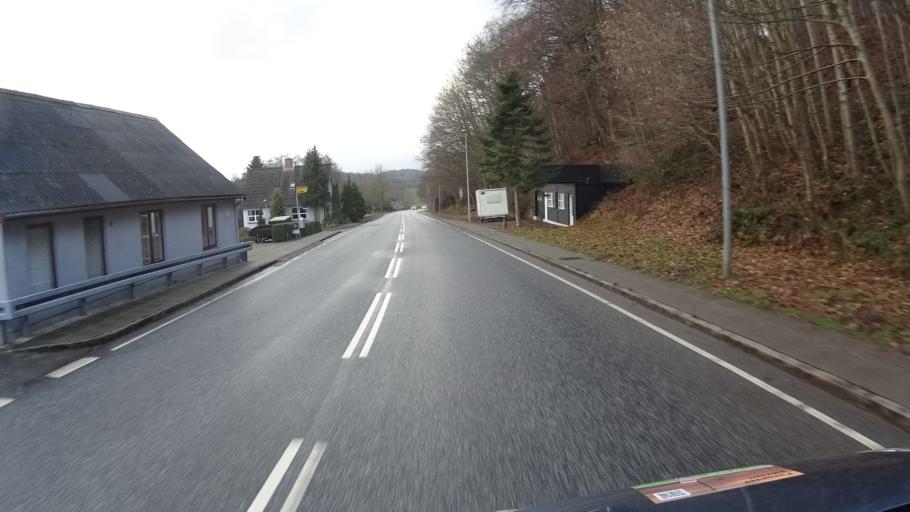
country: DK
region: South Denmark
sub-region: Vejle Kommune
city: Vejle
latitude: 55.7144
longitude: 9.4996
